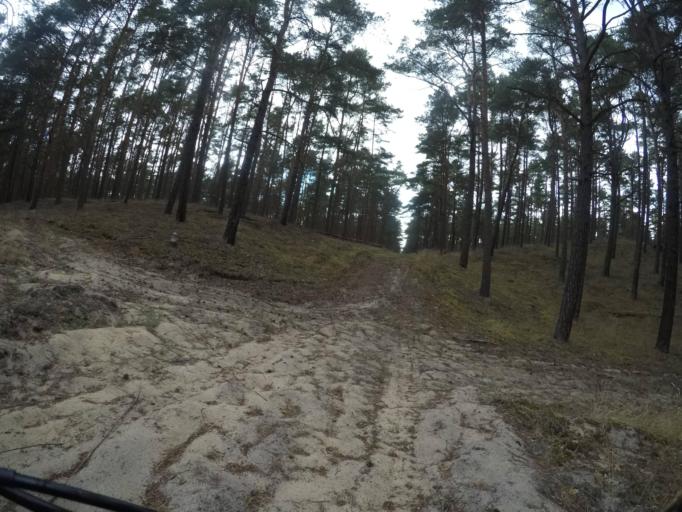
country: DE
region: Lower Saxony
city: Hitzacker
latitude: 53.1941
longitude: 11.0635
